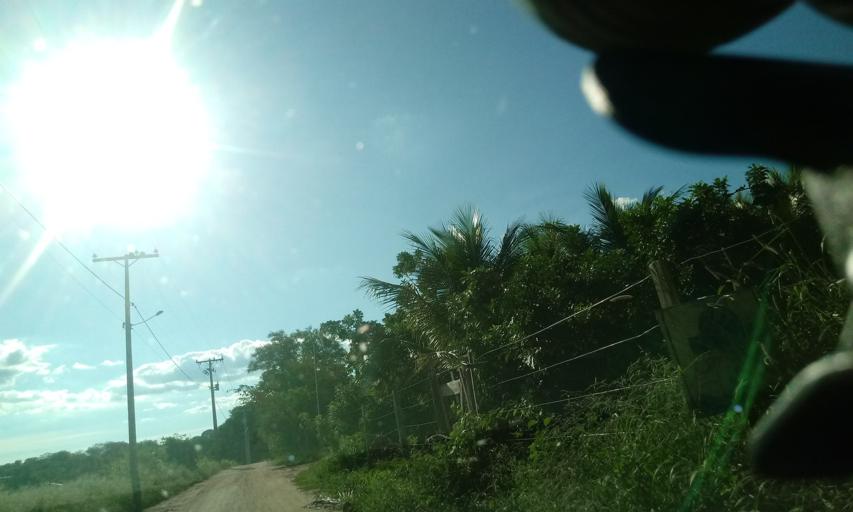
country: BR
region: Bahia
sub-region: Riacho De Santana
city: Riacho de Santana
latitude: -13.7999
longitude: -42.7416
